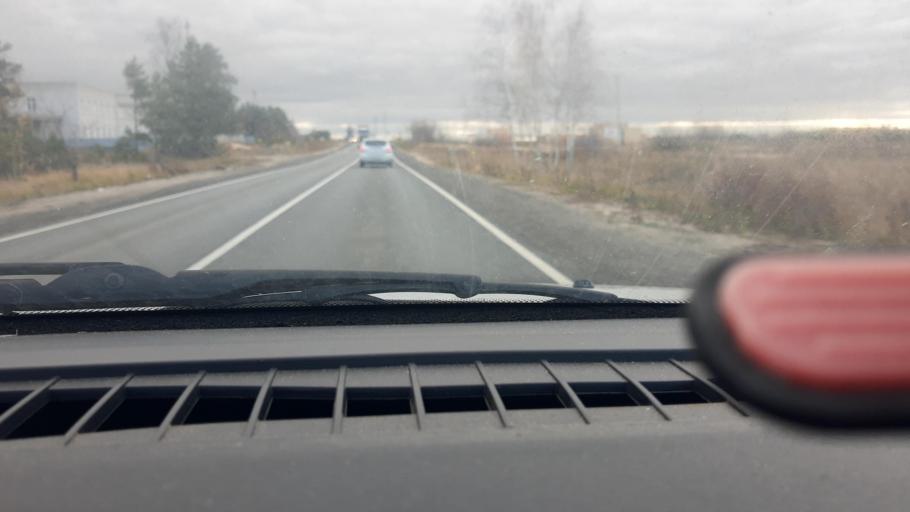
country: RU
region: Nizjnij Novgorod
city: Babino
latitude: 56.2954
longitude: 43.5975
